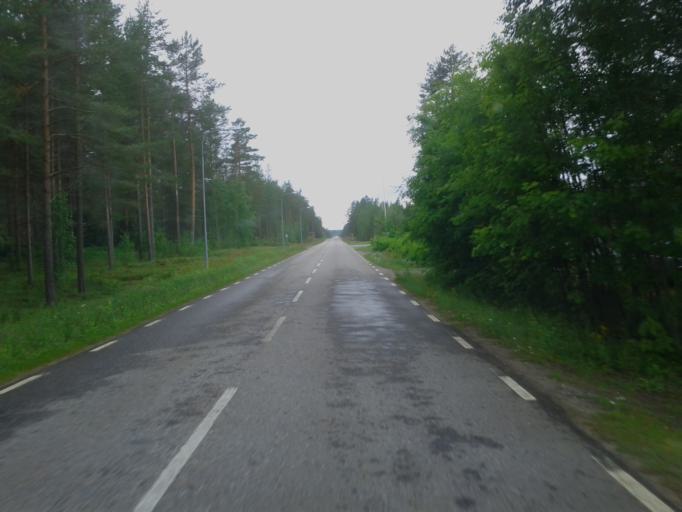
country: SE
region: Vaesterbotten
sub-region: Skelleftea Kommun
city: Kage
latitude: 64.9195
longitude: 20.9485
